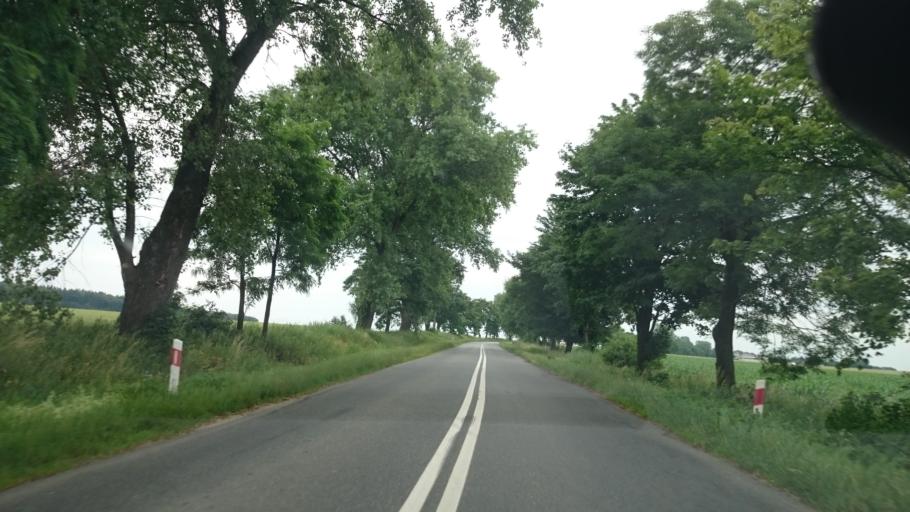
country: PL
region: Lower Silesian Voivodeship
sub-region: Powiat zabkowicki
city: Kamieniec Zabkowicki
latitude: 50.5817
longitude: 16.9030
